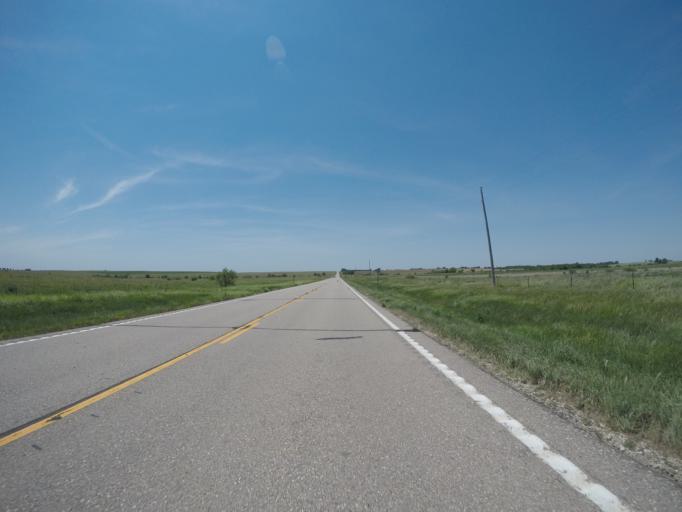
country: US
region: Kansas
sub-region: Dickinson County
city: Solomon
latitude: 39.0305
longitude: -97.3815
